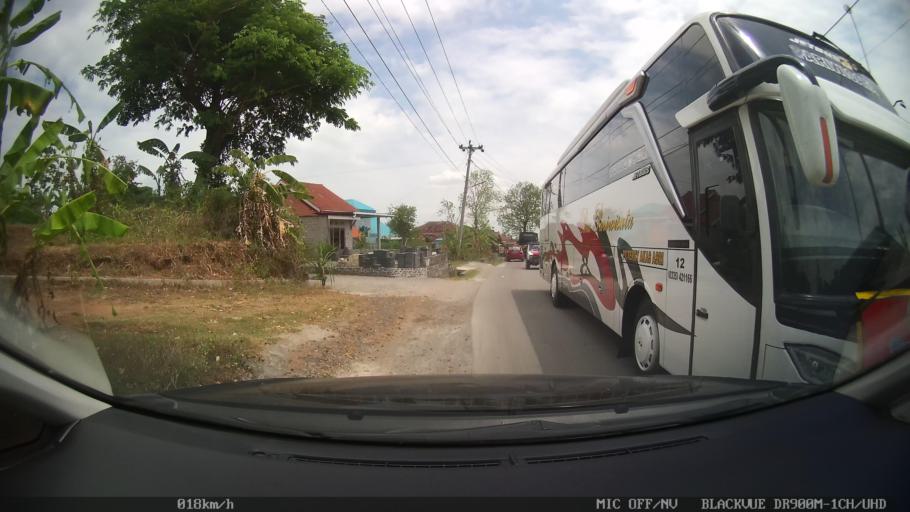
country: ID
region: Central Java
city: Candi Prambanan
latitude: -7.7841
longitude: 110.4987
